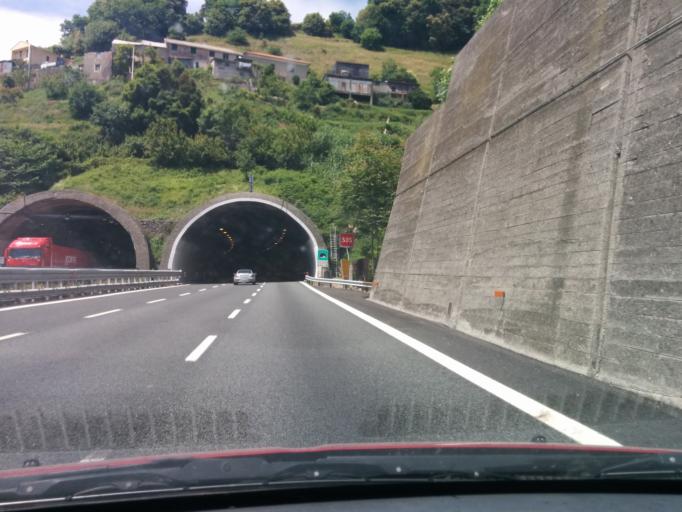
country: IT
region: Liguria
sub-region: Provincia di Genova
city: Mele
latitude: 44.4404
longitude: 8.7355
